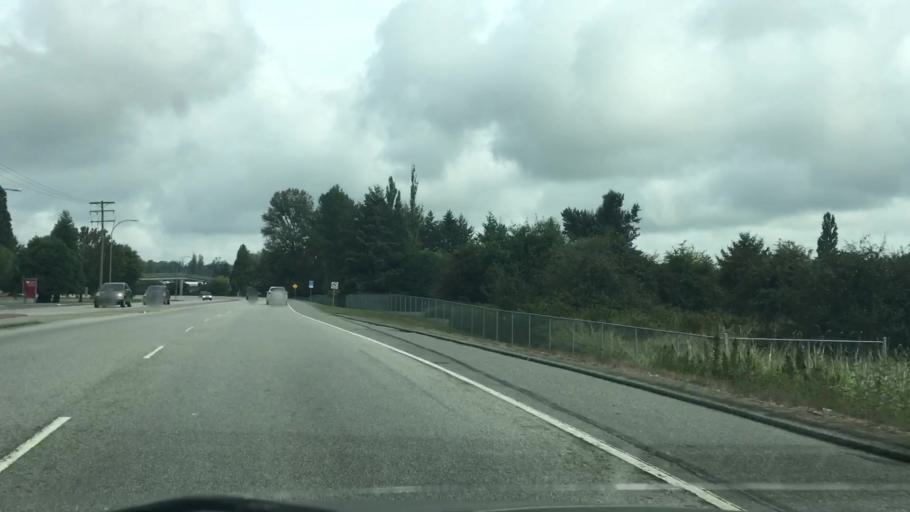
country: CA
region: British Columbia
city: Langley
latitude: 49.1073
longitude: -122.6427
